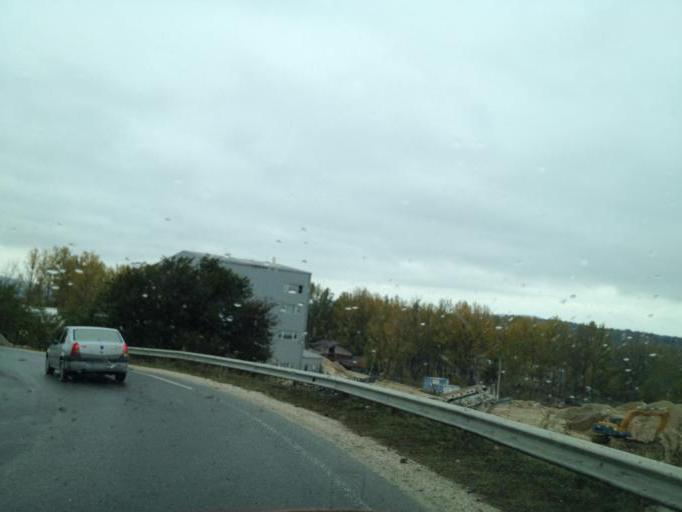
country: RO
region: Arges
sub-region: Comuna Valea Mare-Pravat
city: Valea Mare Pravat
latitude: 45.2940
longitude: 25.1196
